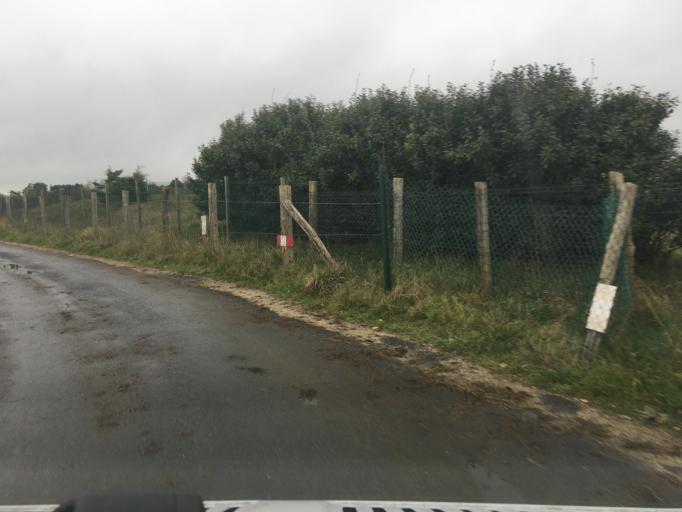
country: FR
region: Lower Normandy
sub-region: Departement de la Manche
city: Sainte-Mere-Eglise
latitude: 49.4805
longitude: -1.2547
